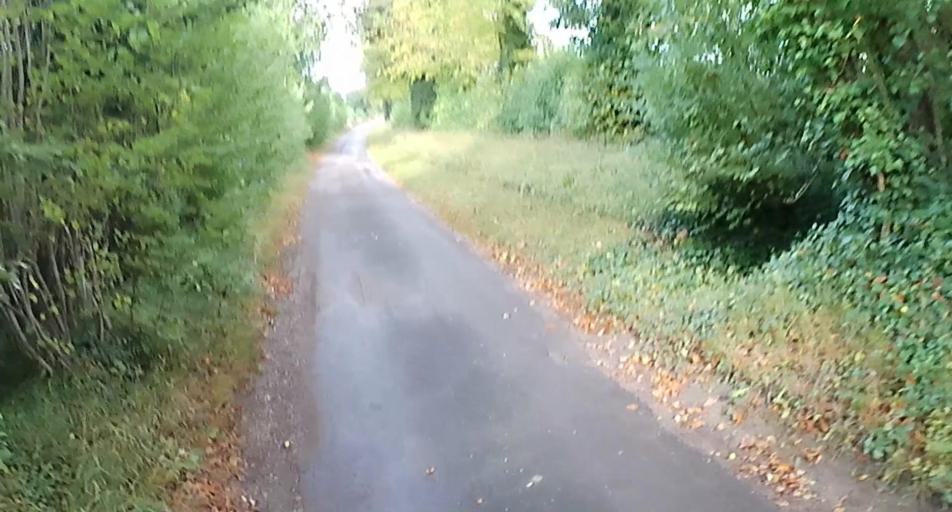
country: GB
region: England
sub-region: Hampshire
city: Kingsclere
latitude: 51.2775
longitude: -1.1981
